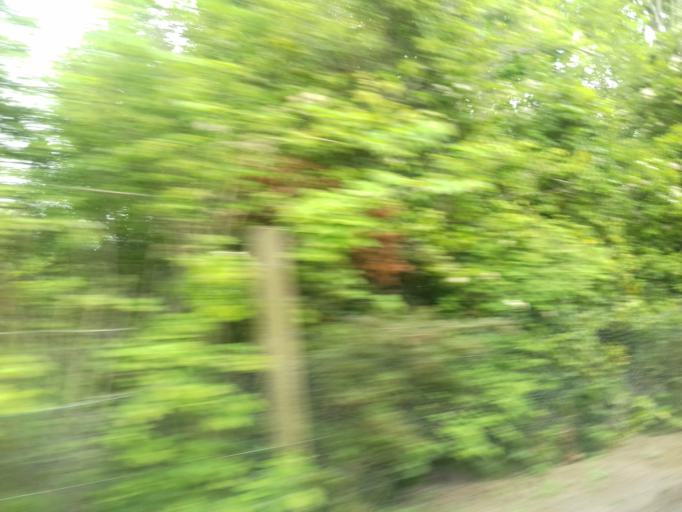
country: IE
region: Leinster
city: Donabate
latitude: 53.4889
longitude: -6.1782
